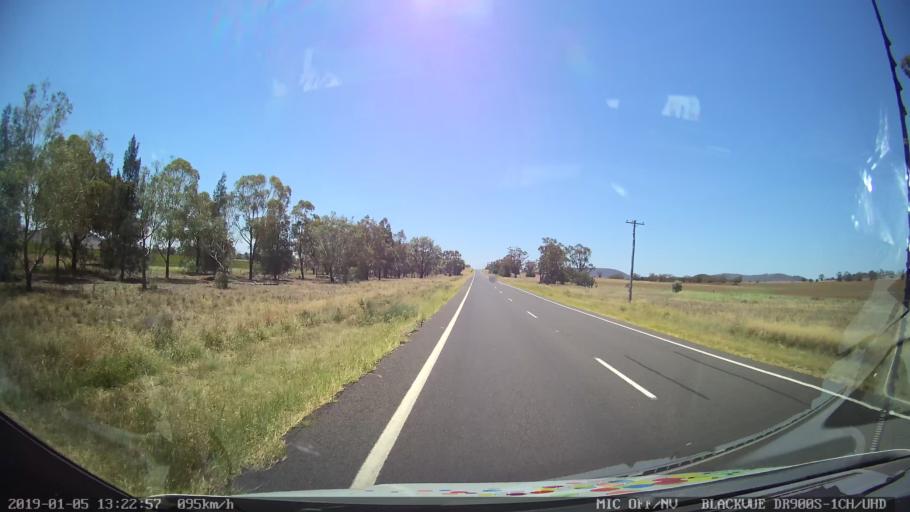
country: AU
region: New South Wales
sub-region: Gunnedah
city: Gunnedah
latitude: -31.0819
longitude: 149.9688
